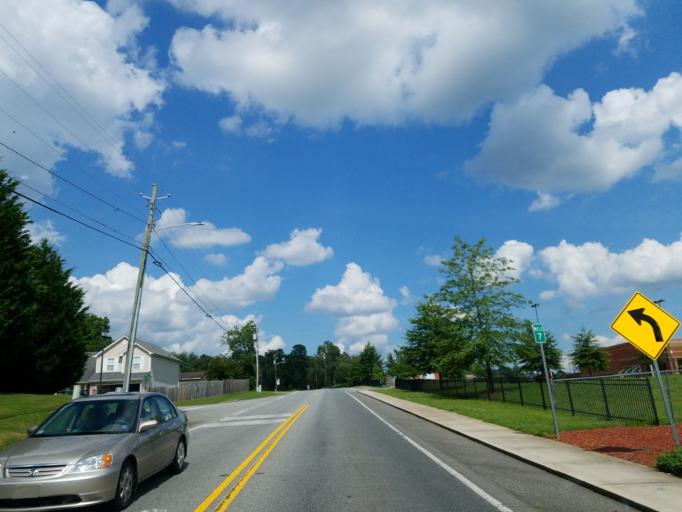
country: US
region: Georgia
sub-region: Dawson County
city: Dawsonville
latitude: 34.4212
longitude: -84.1143
